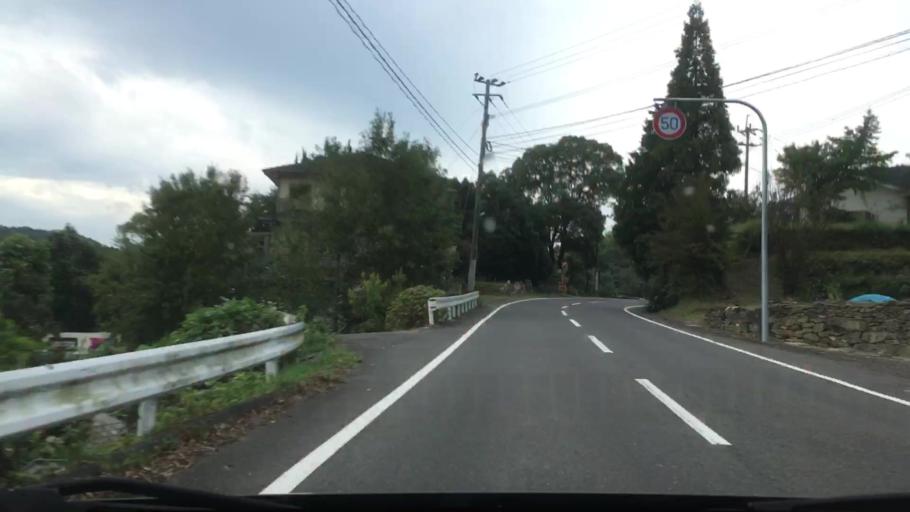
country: JP
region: Nagasaki
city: Sasebo
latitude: 32.9859
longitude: 129.7193
